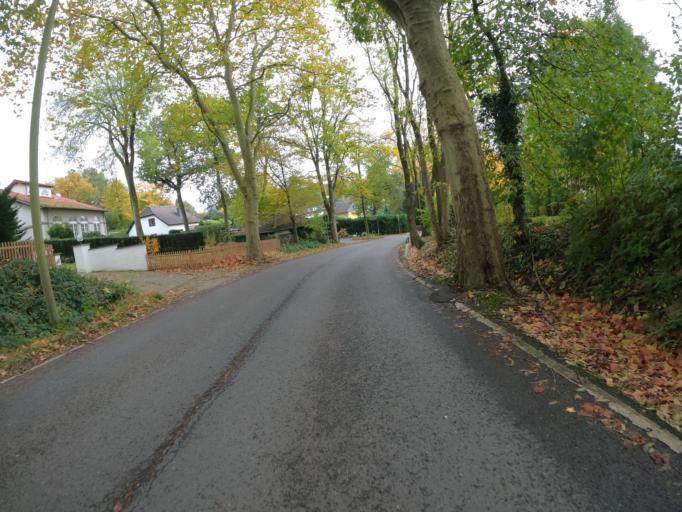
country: DE
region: North Rhine-Westphalia
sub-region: Regierungsbezirk Dusseldorf
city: Wuppertal
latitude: 51.2700
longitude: 7.1094
